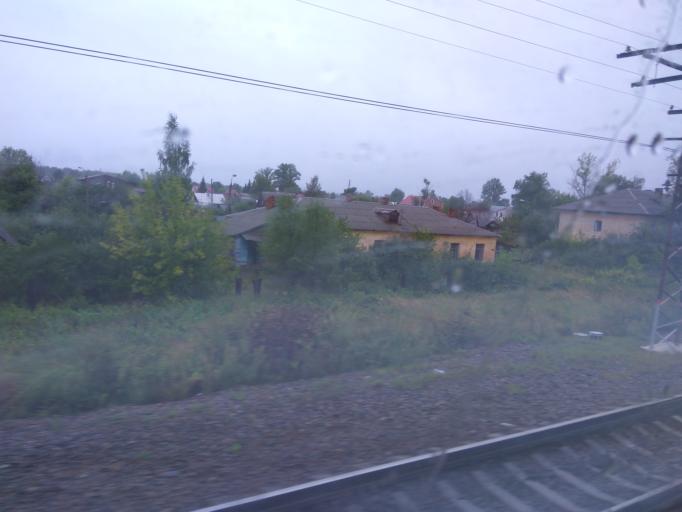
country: RU
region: Moskovskaya
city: Zhilevo
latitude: 54.9812
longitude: 38.0336
